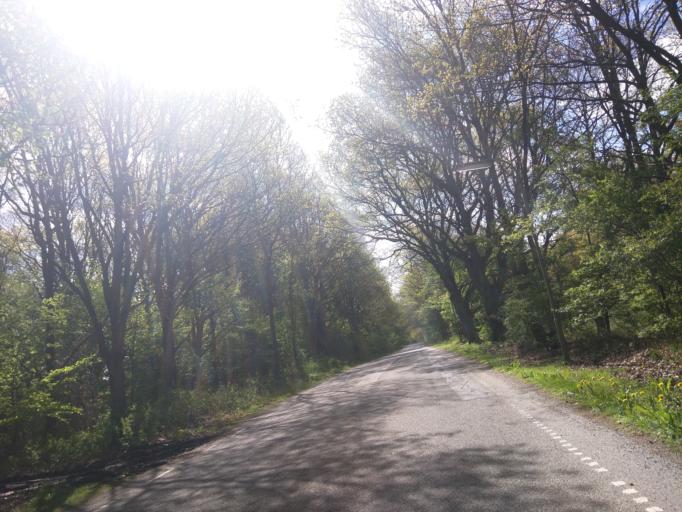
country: DK
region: Central Jutland
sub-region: Viborg Kommune
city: Viborg
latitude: 56.4081
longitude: 9.4238
